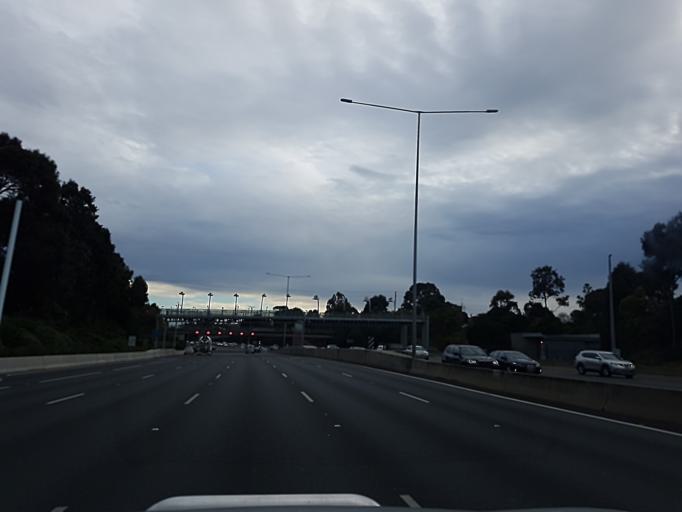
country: AU
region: Victoria
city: Brunswick West
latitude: -37.7595
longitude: 144.9378
